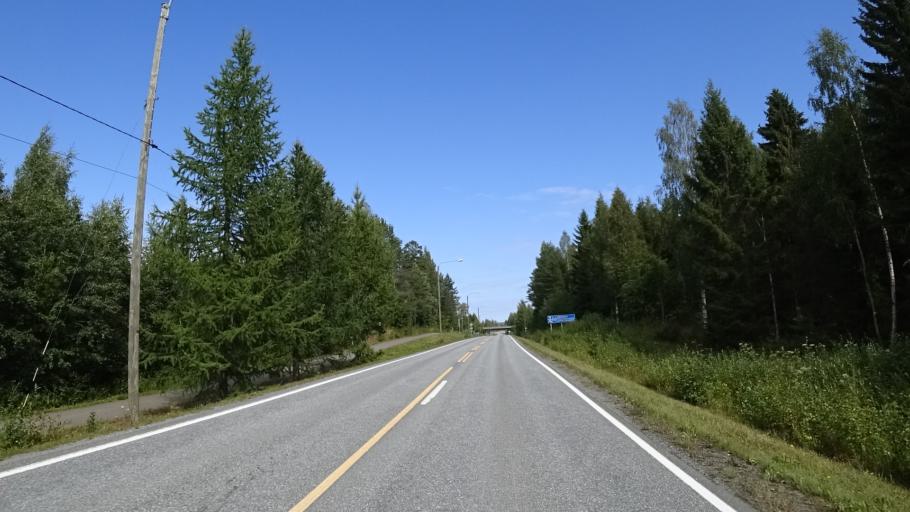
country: FI
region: North Karelia
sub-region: Joensuu
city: Pyhaeselkae
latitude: 62.4743
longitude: 29.9524
